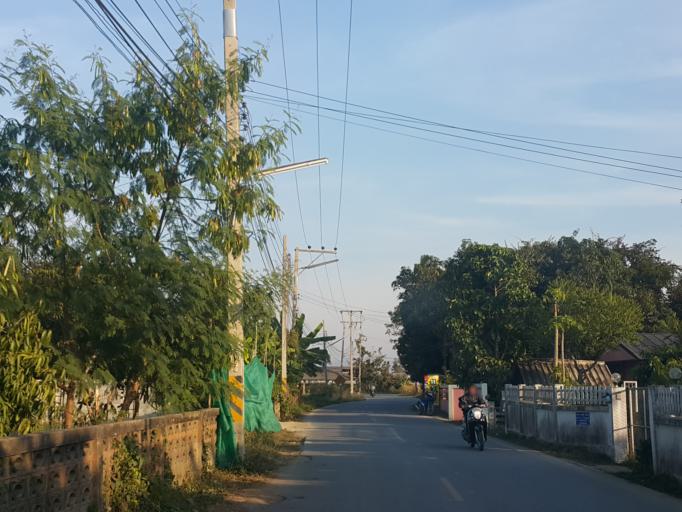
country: TH
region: Chiang Mai
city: San Sai
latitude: 18.8284
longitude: 99.0814
